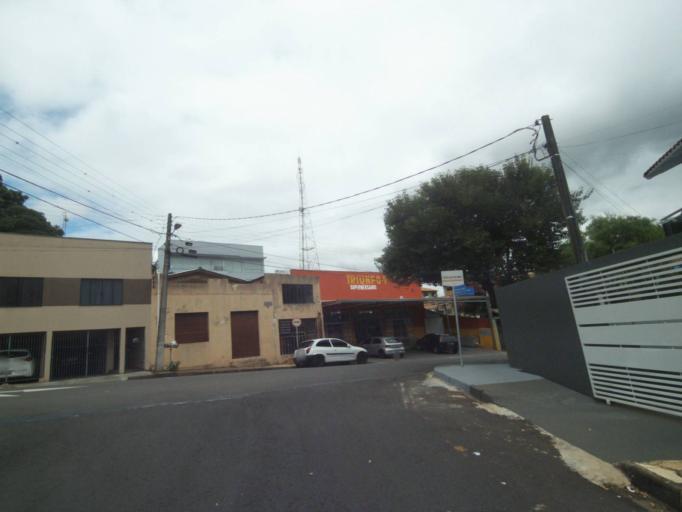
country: BR
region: Parana
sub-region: Telemaco Borba
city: Telemaco Borba
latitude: -24.3289
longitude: -50.6151
